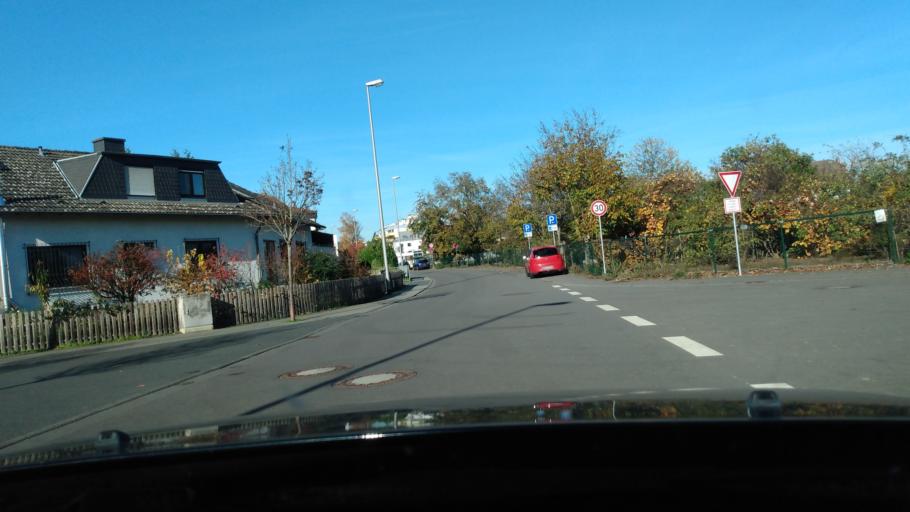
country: DE
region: Hesse
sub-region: Regierungsbezirk Darmstadt
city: Hattersheim
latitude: 50.0808
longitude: 8.4769
